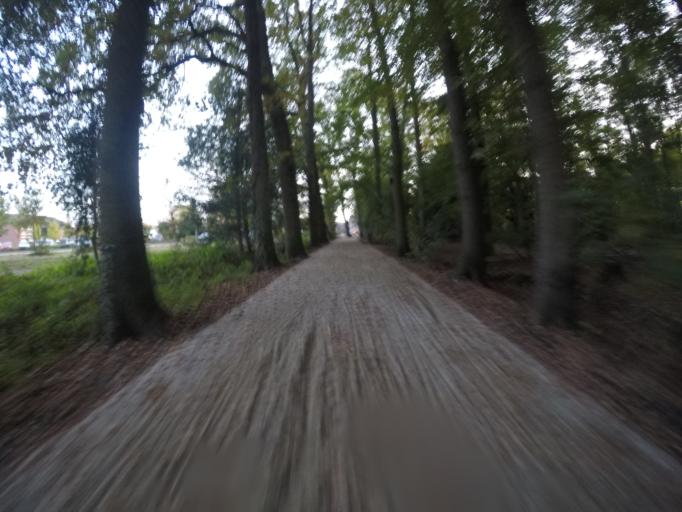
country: DE
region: North Rhine-Westphalia
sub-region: Regierungsbezirk Munster
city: Rhede
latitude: 51.8404
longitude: 6.6905
